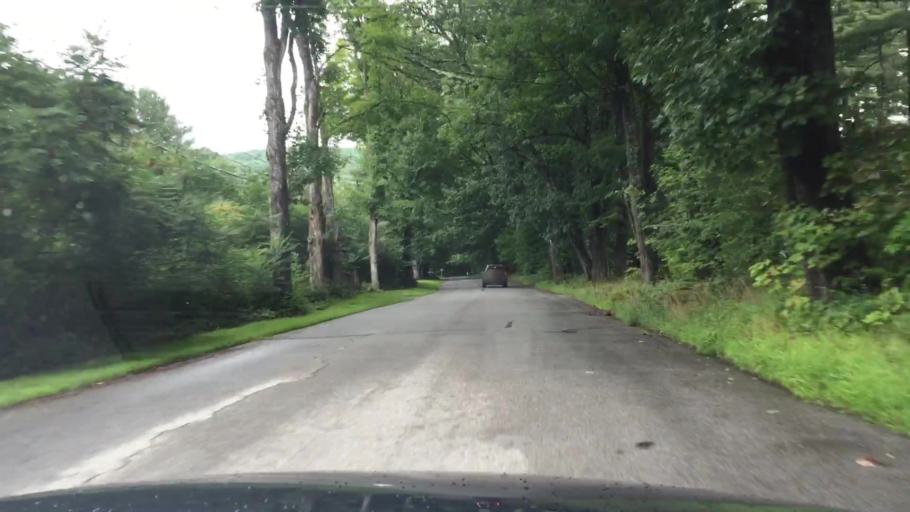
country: US
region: New Hampshire
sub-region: Grafton County
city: Holderness
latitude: 43.7294
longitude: -71.5788
